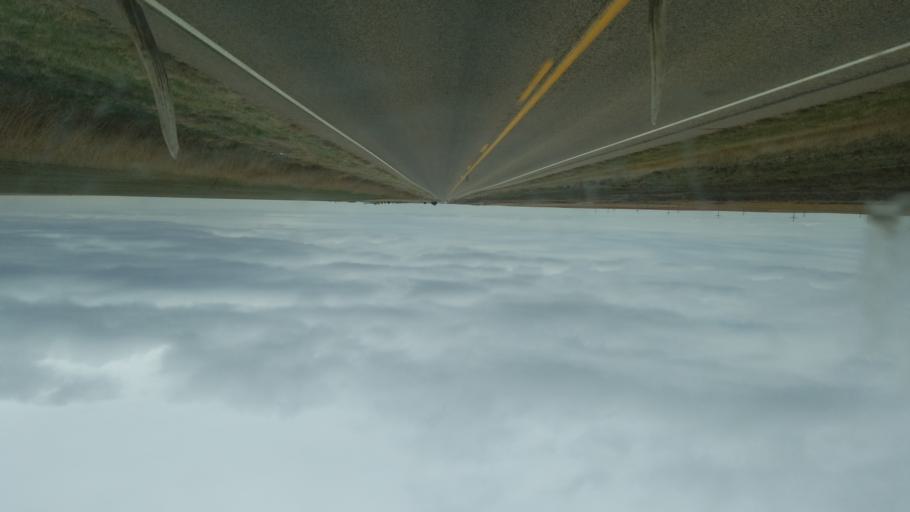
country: US
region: Colorado
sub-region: Cheyenne County
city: Cheyenne Wells
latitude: 38.8256
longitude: -102.3211
